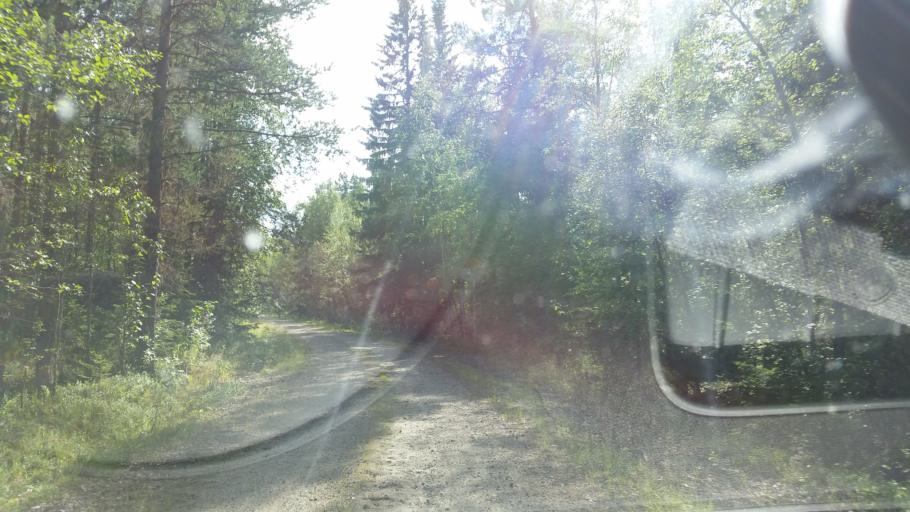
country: SE
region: Vaesternorrland
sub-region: Ange Kommun
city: Ange
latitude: 62.2338
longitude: 15.7098
